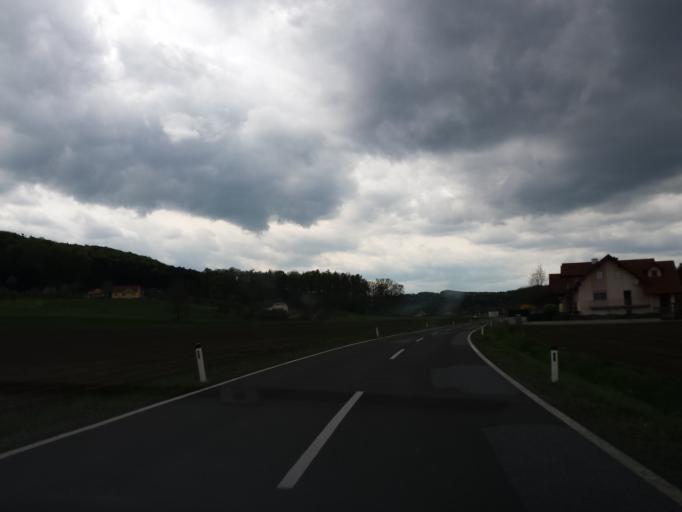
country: AT
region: Styria
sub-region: Politischer Bezirk Suedoststeiermark
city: Hatzendorf
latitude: 46.9881
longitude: 15.9798
